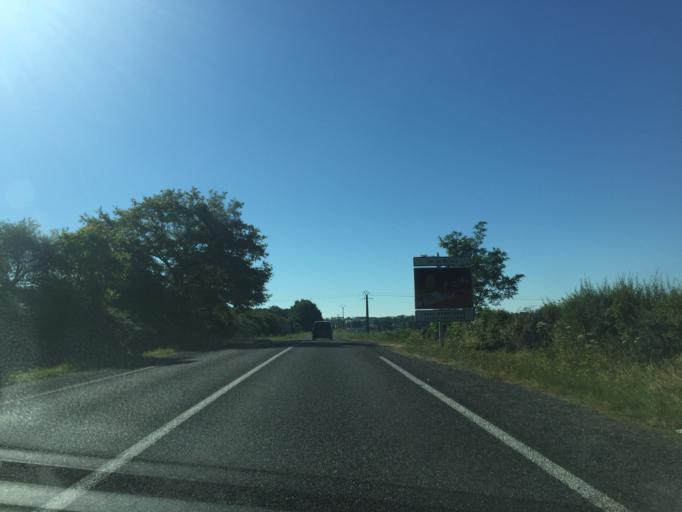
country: FR
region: Auvergne
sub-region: Departement de l'Allier
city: Dompierre-sur-Besbre
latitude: 46.5365
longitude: 3.6569
